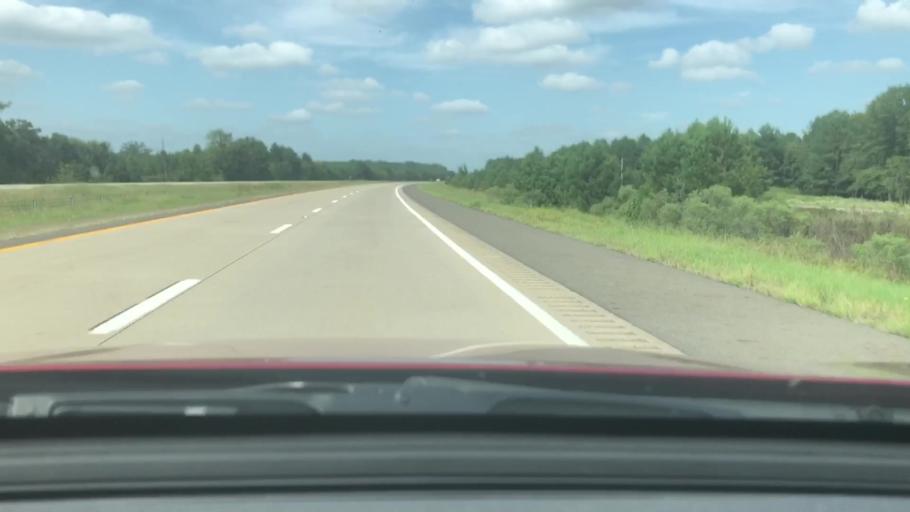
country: US
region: Texas
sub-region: Cass County
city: Queen City
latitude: 33.1990
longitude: -93.8779
